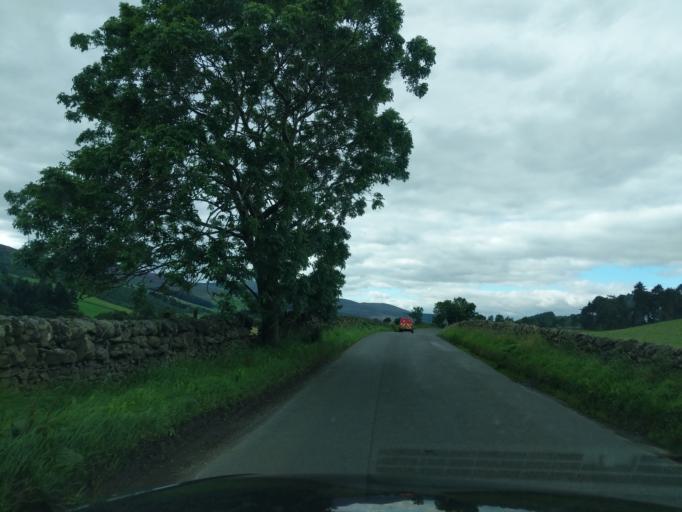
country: GB
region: Scotland
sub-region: The Scottish Borders
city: Peebles
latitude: 55.6451
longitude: -3.2774
